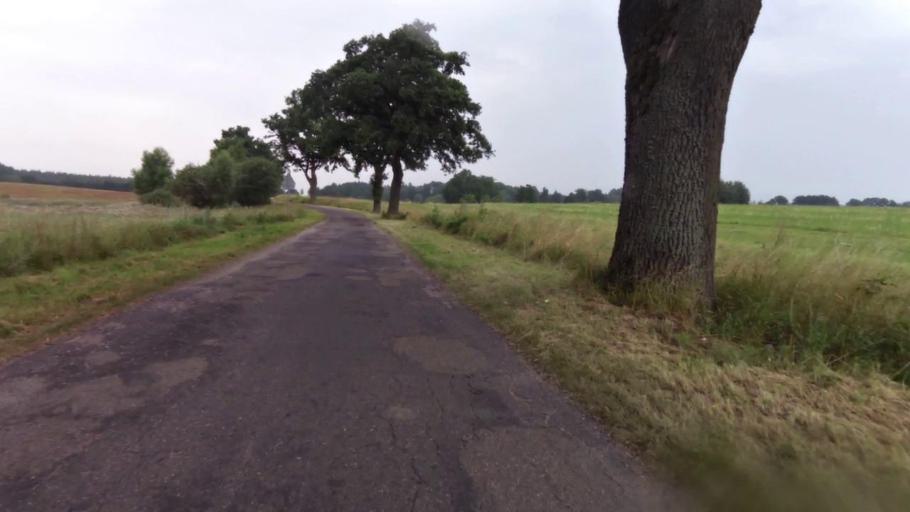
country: PL
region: West Pomeranian Voivodeship
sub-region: Powiat lobeski
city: Wegorzyno
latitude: 53.5108
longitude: 15.6492
